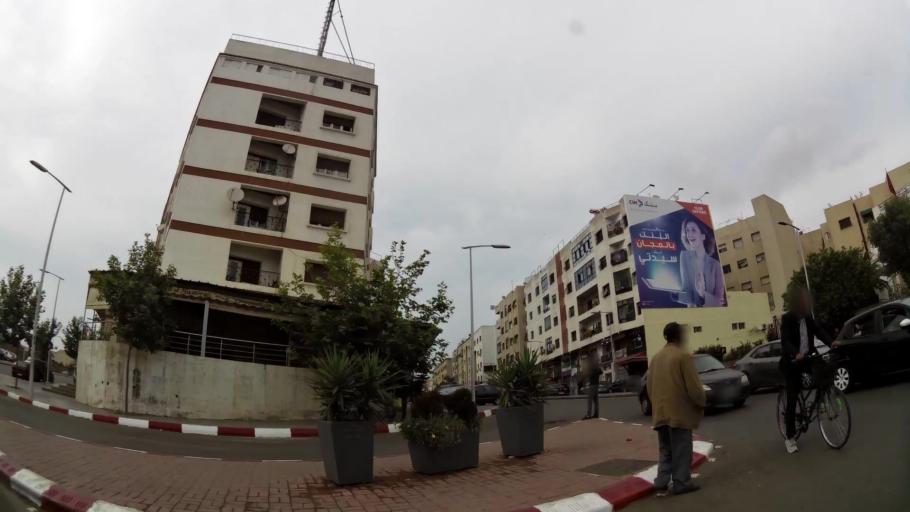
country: MA
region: Rabat-Sale-Zemmour-Zaer
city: Sale
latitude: 34.0362
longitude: -6.8063
